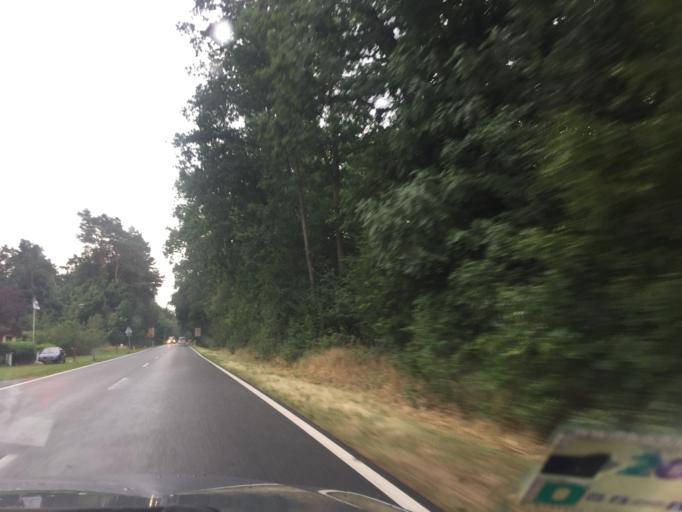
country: DE
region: Brandenburg
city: Liebenwalde
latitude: 52.8330
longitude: 13.4076
